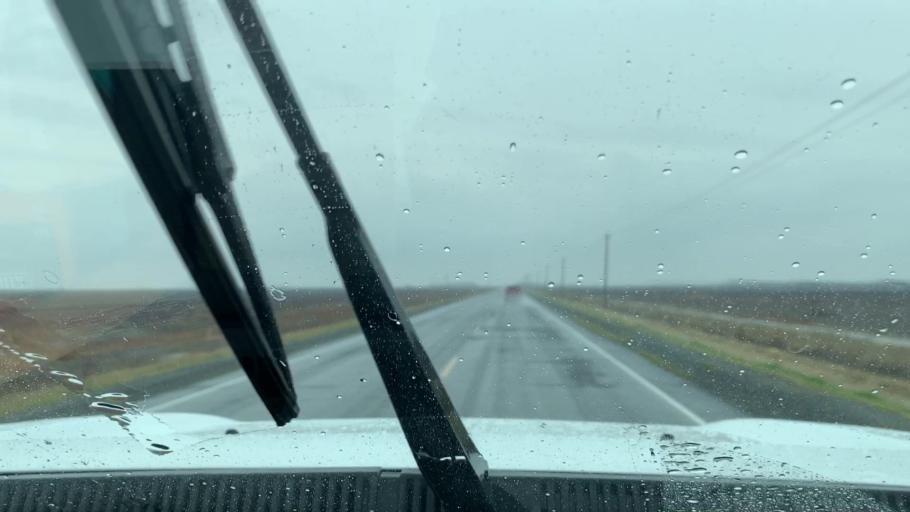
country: US
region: California
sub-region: Tulare County
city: Alpaugh
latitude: 35.9299
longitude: -119.4333
